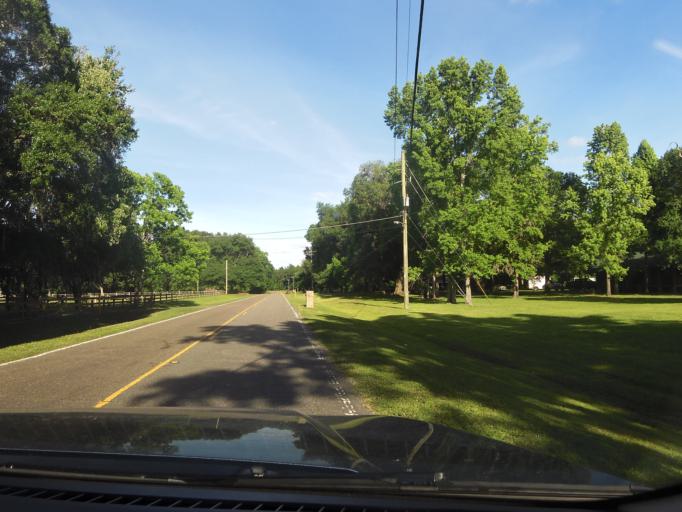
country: US
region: Florida
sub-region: Nassau County
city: Nassau Village-Ratliff
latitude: 30.4673
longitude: -81.8122
